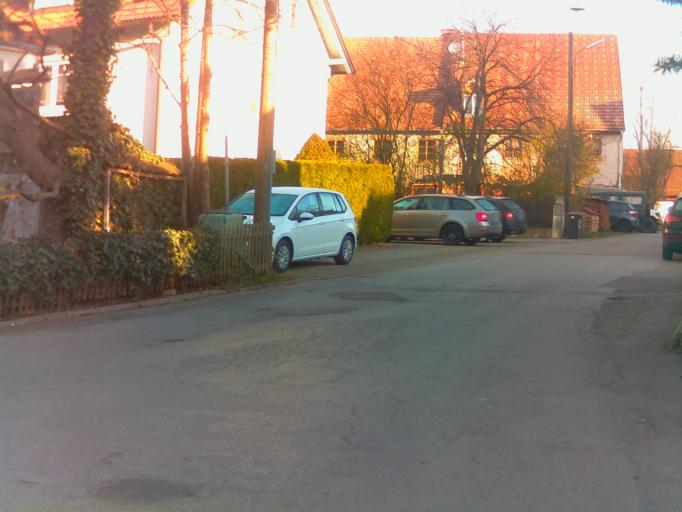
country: DE
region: Bavaria
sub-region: Upper Bavaria
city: Geltendorf
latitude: 48.1243
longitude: 11.0264
